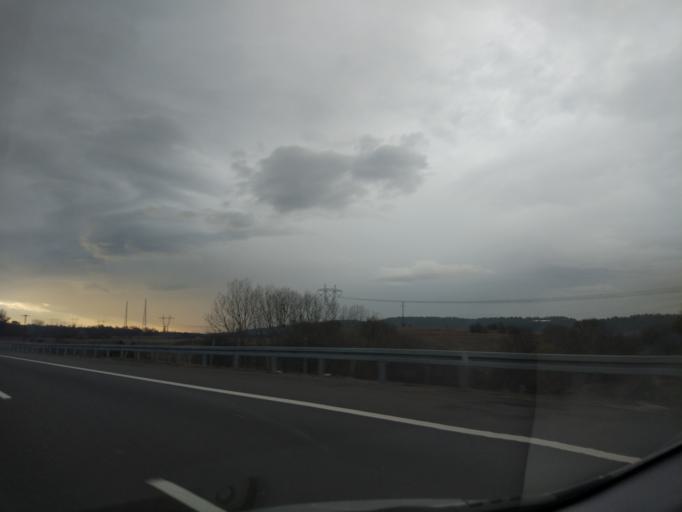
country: TR
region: Bolu
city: Yenicaga
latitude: 40.7529
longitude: 31.9454
